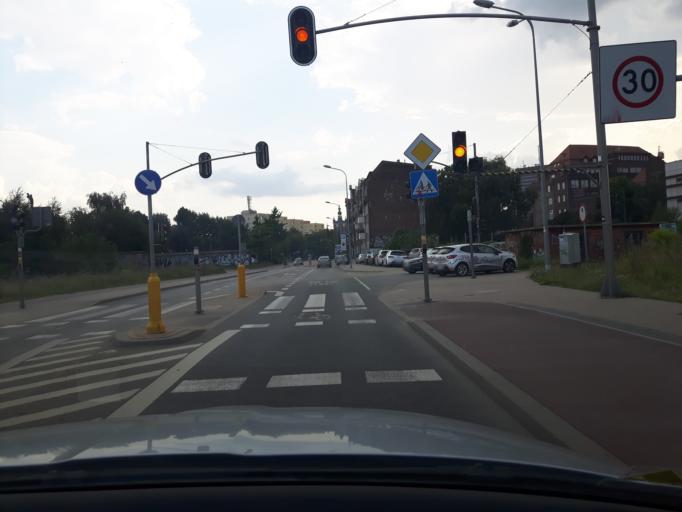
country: PL
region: Pomeranian Voivodeship
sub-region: Gdansk
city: Gdansk
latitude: 54.3597
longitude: 18.6567
